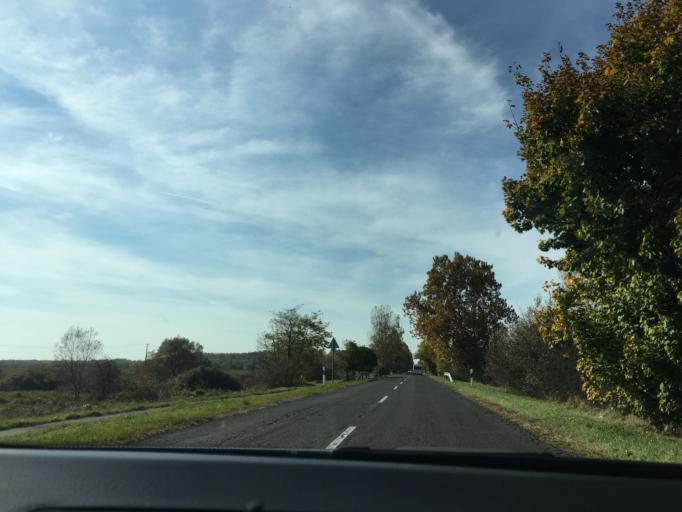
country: HU
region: Hajdu-Bihar
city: Vamospercs
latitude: 47.5263
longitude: 21.9603
